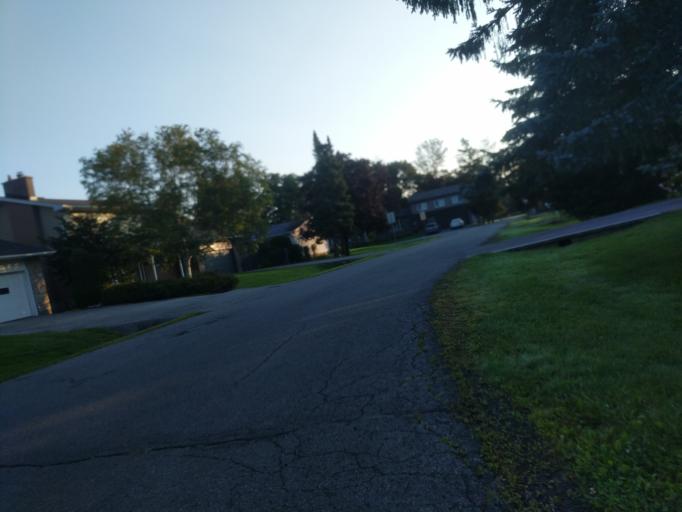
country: CA
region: Ontario
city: Bells Corners
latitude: 45.3454
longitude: -75.8257
